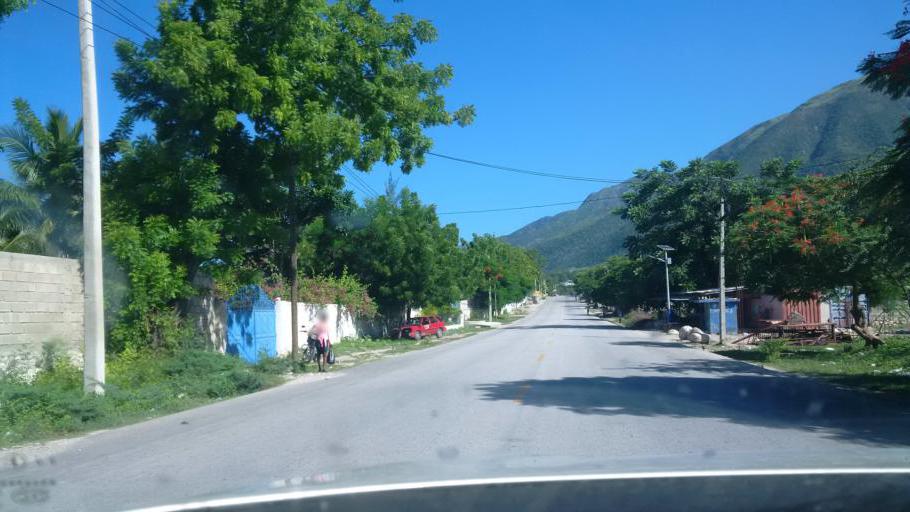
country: HT
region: Artibonite
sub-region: Arrondissement de Saint-Marc
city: Verrettes
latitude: 18.8836
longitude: -72.6167
